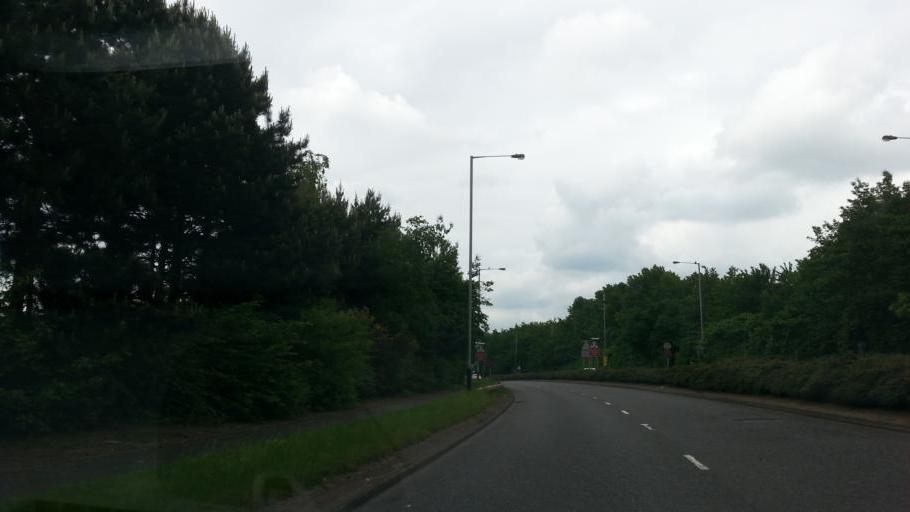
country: GB
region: England
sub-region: Wolverhampton
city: Bilston
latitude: 52.5597
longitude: -2.0847
